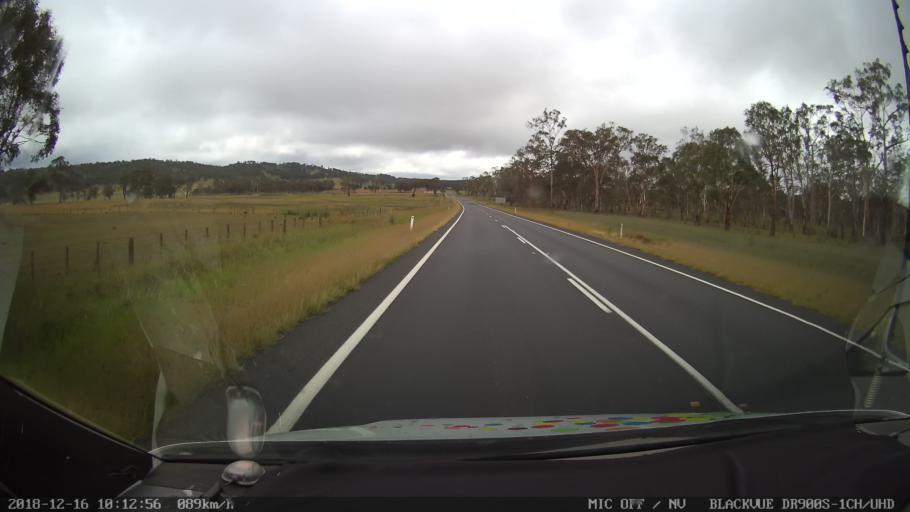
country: AU
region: New South Wales
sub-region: Glen Innes Severn
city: Glen Innes
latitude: -29.3019
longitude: 151.9467
